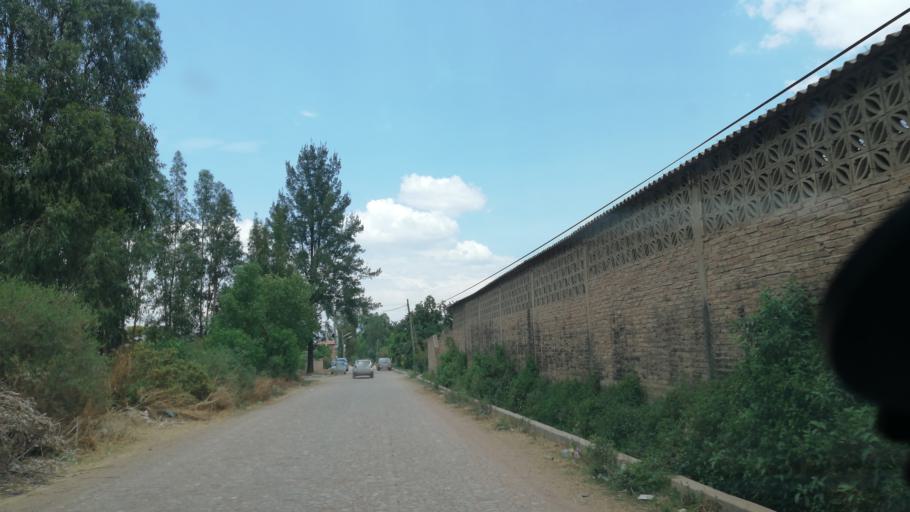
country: BO
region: Cochabamba
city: Cochabamba
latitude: -17.3573
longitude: -66.2211
